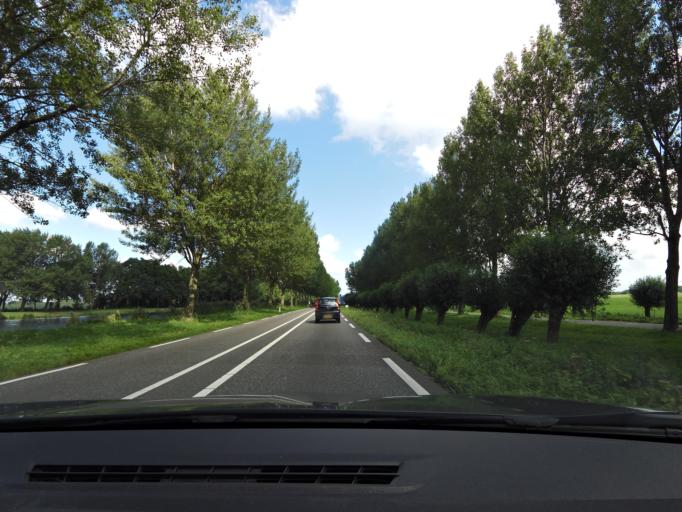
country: NL
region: South Holland
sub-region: Gemeente Alphen aan den Rijn
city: Alphen aan den Rijn
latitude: 52.1325
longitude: 4.6882
